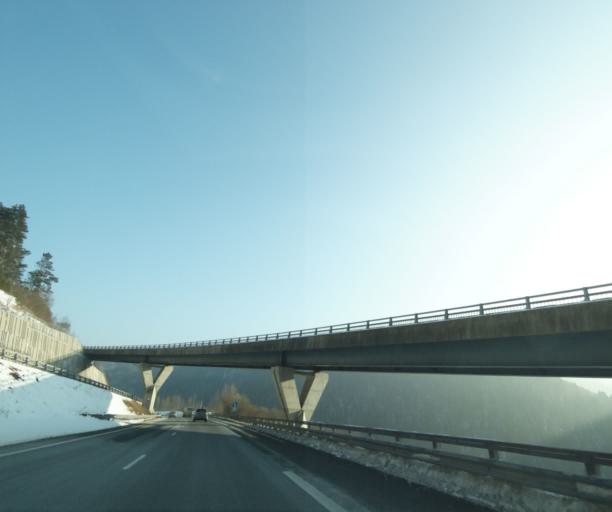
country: FR
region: Rhone-Alpes
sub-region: Departement de l'Ain
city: Nantua
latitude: 46.1663
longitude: 5.6950
